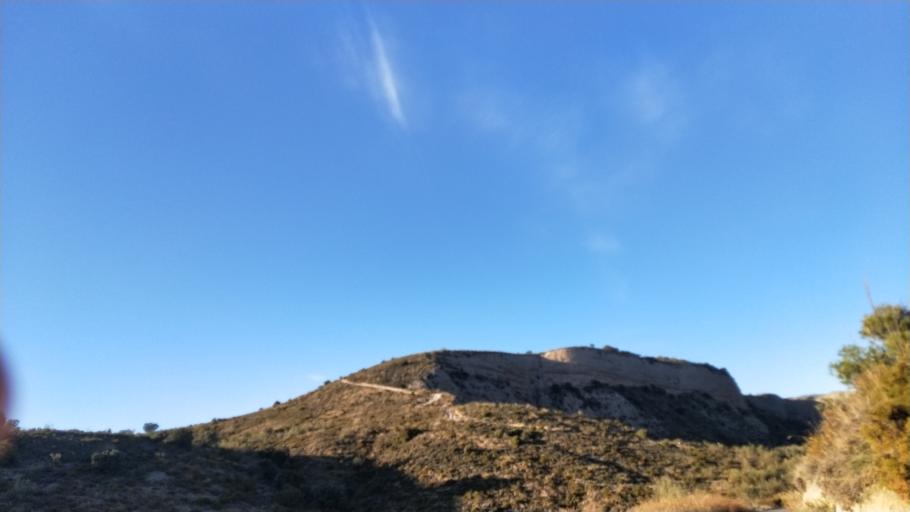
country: ES
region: Andalusia
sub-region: Provincia de Granada
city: Dudar
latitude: 37.1948
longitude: -3.5011
